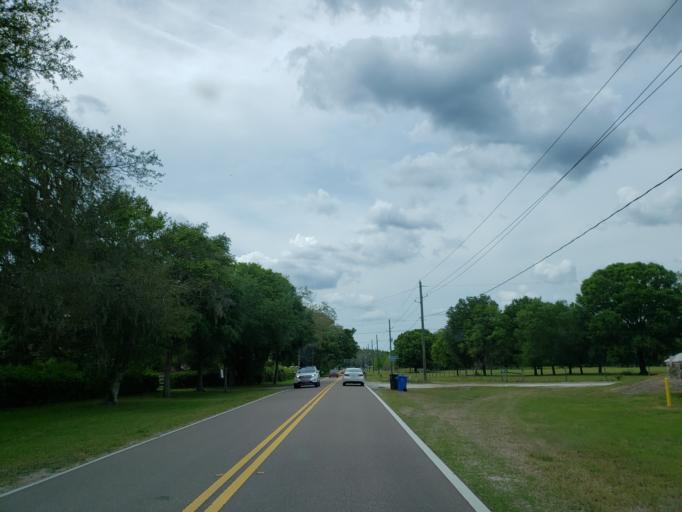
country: US
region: Florida
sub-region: Hillsborough County
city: Keystone
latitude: 28.1250
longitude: -82.6134
